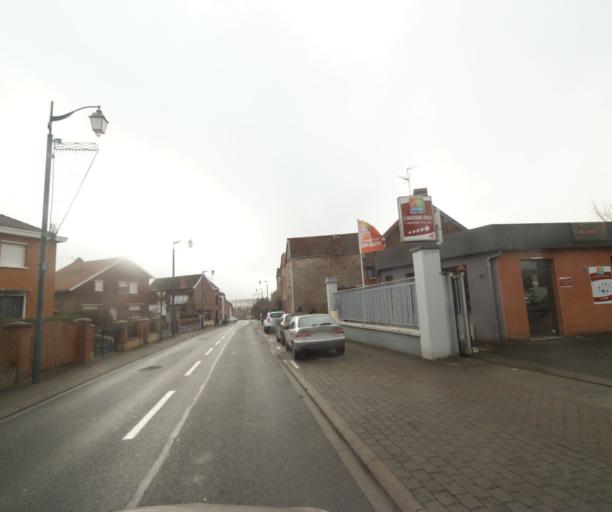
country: FR
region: Nord-Pas-de-Calais
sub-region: Departement du Nord
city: Aulnoy-lez-Valenciennes
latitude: 50.3352
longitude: 3.5276
